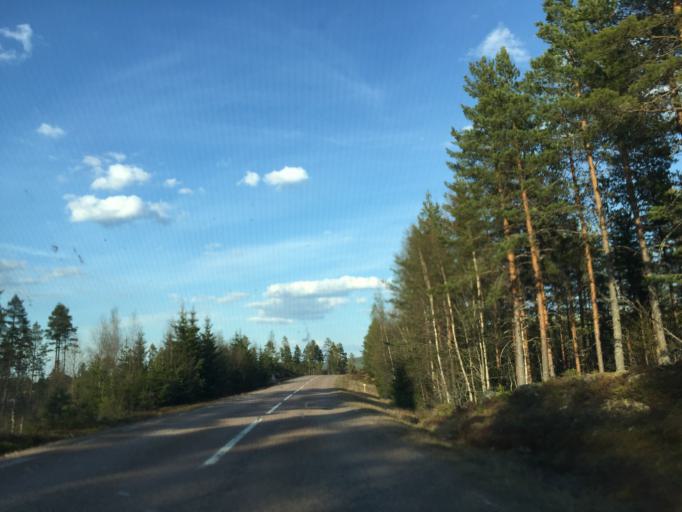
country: SE
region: Dalarna
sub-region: Vansbro Kommun
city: Jarna
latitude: 60.6395
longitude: 14.5686
